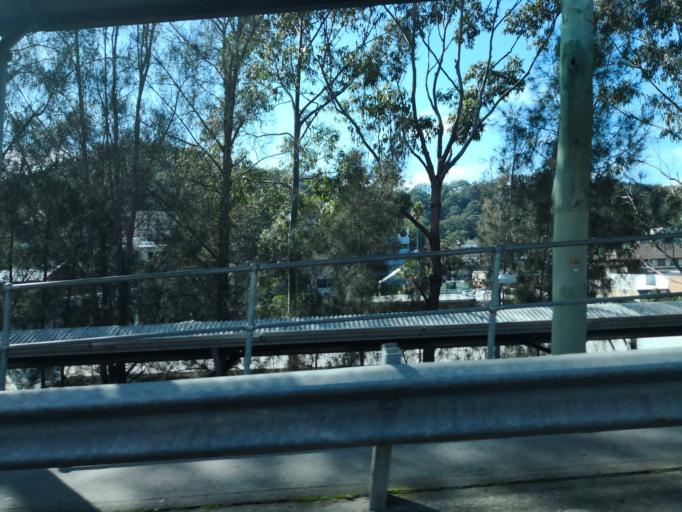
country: AU
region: New South Wales
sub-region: Gosford Shire
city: Gosford
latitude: -33.4239
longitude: 151.3412
